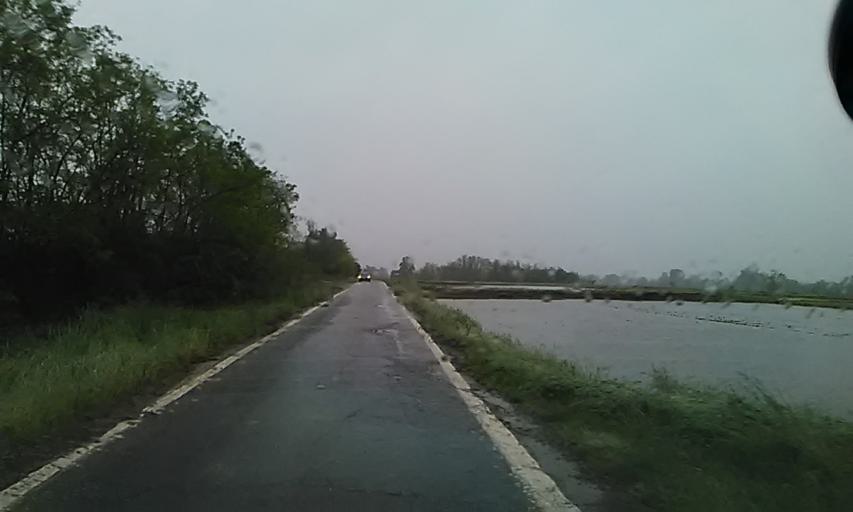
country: IT
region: Piedmont
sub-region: Provincia di Vercelli
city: San Giacomo Vercellese
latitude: 45.4879
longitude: 8.3369
